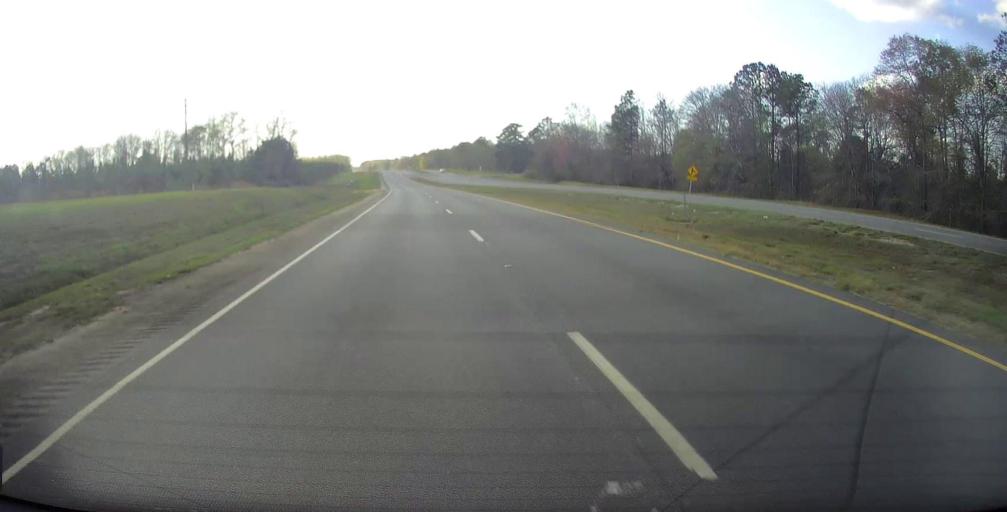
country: US
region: Georgia
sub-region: Telfair County
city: Helena
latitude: 32.1053
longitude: -82.9778
